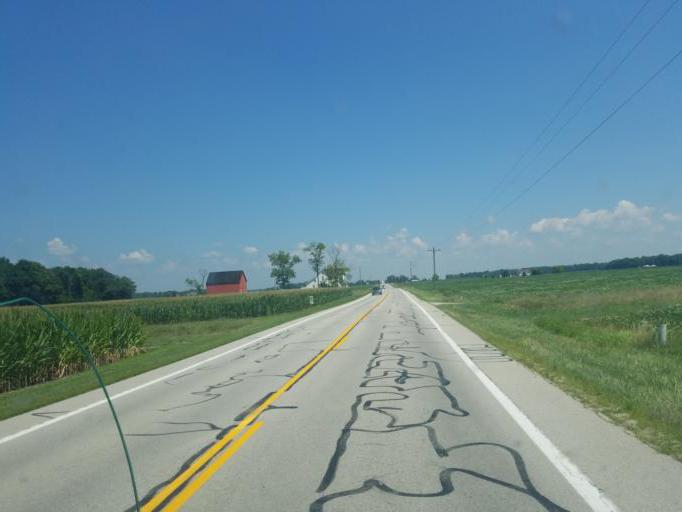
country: US
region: Ohio
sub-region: Shelby County
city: Anna
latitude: 40.3953
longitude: -84.1277
